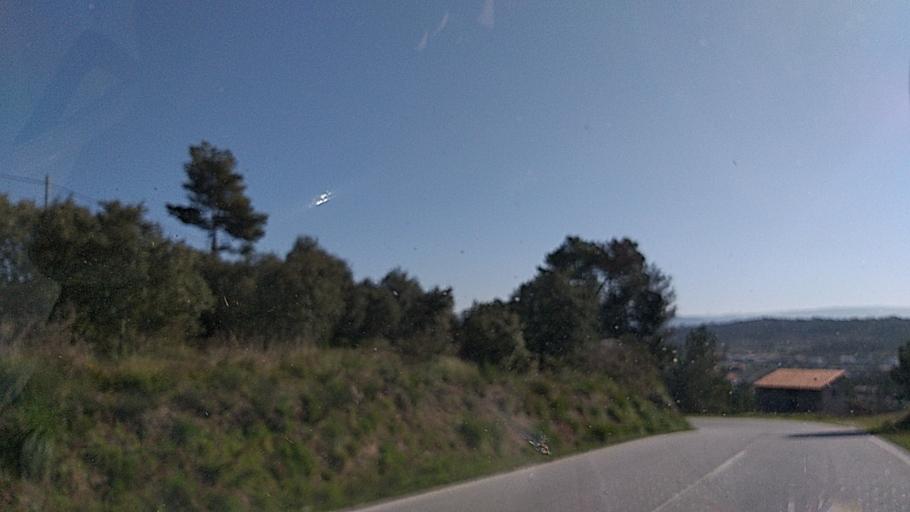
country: PT
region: Guarda
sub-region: Celorico da Beira
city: Celorico da Beira
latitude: 40.6704
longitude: -7.3908
